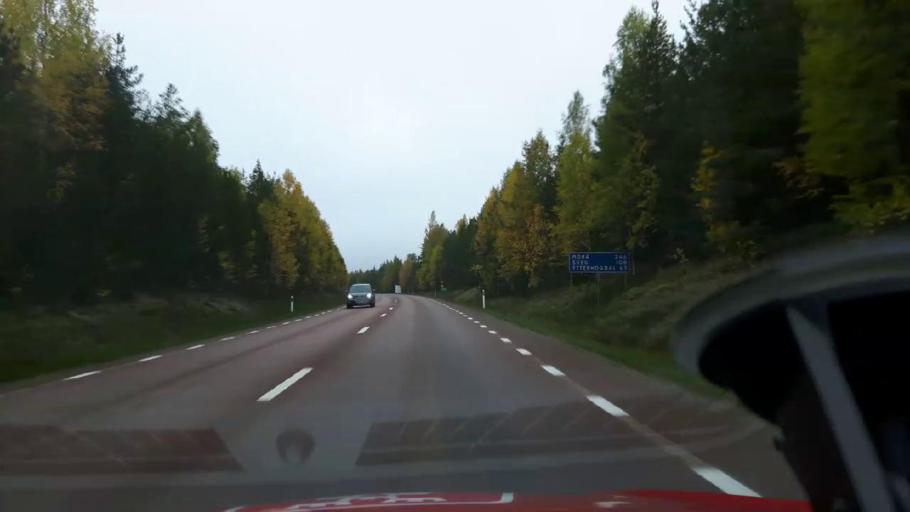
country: SE
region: Jaemtland
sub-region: Bergs Kommun
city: Hoverberg
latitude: 62.6338
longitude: 14.3675
